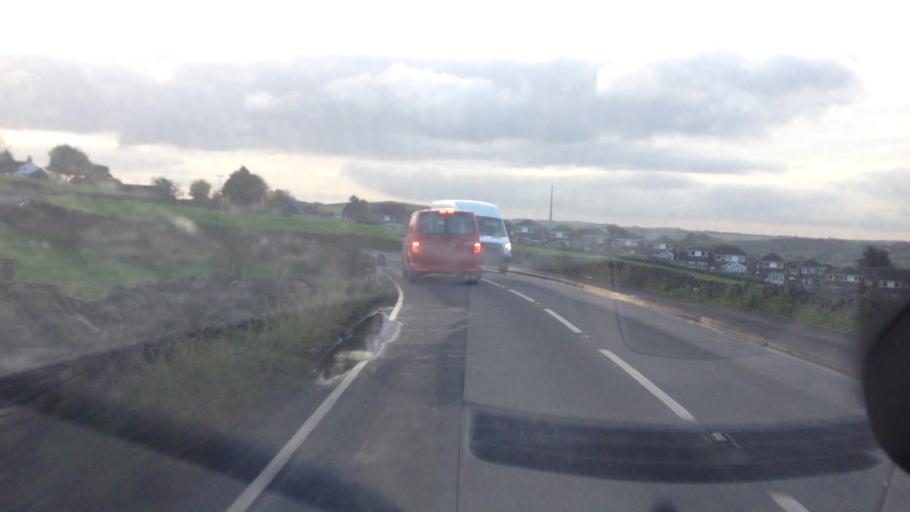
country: GB
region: England
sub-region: Kirklees
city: Mirfield
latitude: 53.6663
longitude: -1.7310
